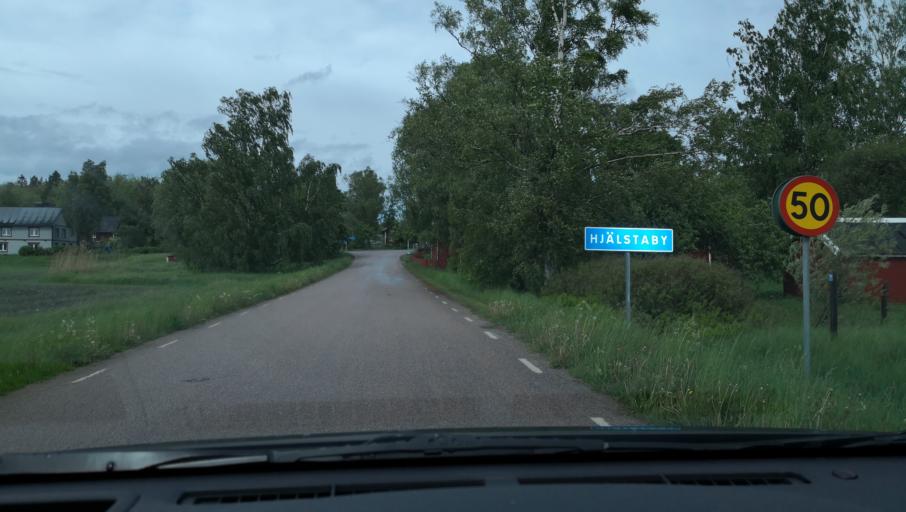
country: SE
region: Uppsala
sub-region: Enkopings Kommun
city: Orsundsbro
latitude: 59.6875
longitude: 17.3798
